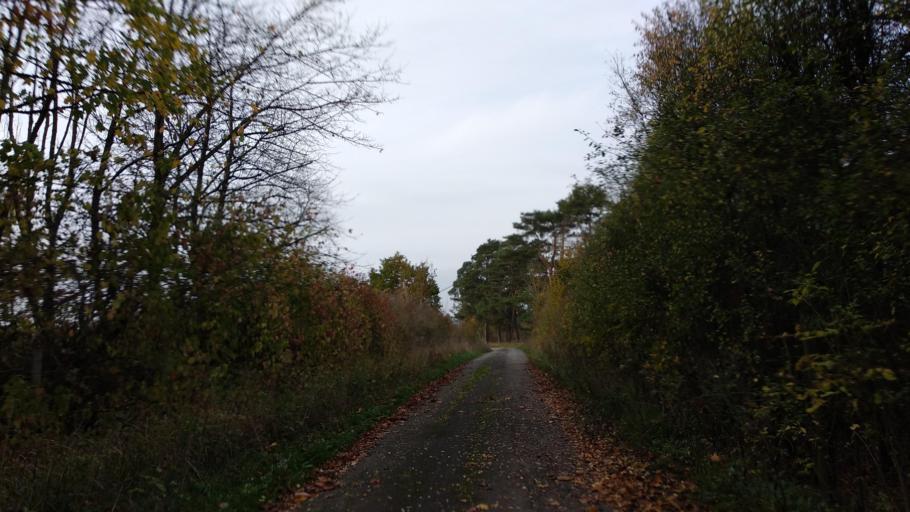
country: DE
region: North Rhine-Westphalia
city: Beverungen
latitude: 51.6882
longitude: 9.3339
